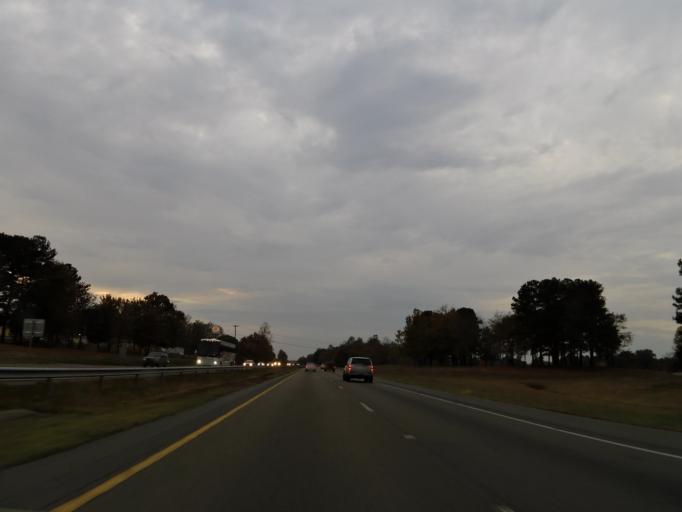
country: US
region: North Carolina
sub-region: Burke County
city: Icard
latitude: 35.7194
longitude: -81.4655
